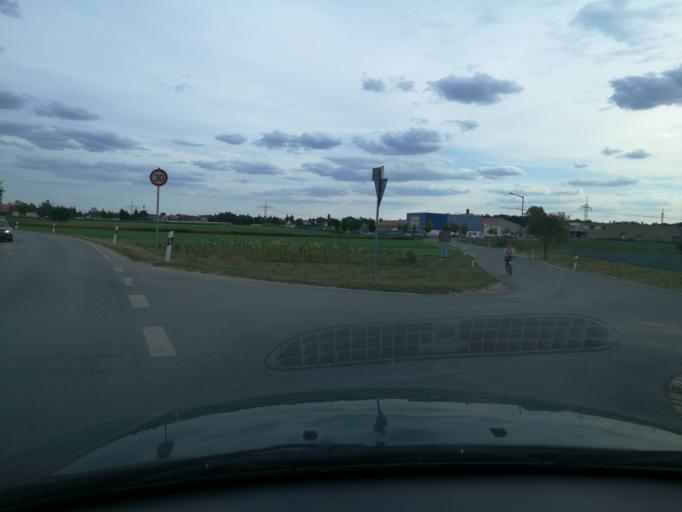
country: DE
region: Bavaria
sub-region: Regierungsbezirk Mittelfranken
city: Furth
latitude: 49.5061
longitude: 11.0047
